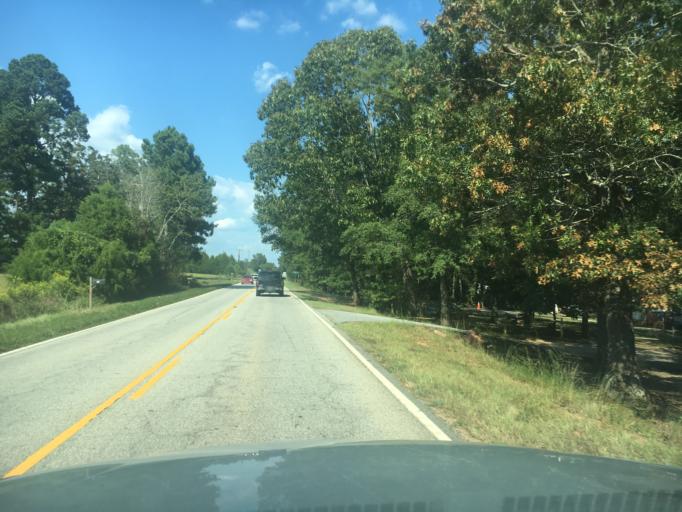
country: US
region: South Carolina
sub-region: Anderson County
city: Pendleton
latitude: 34.5995
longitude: -82.7946
